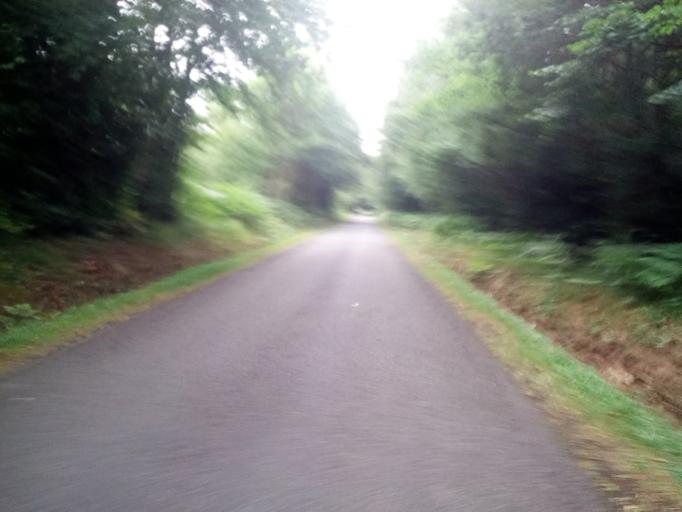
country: FR
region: Lower Normandy
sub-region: Departement du Calvados
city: Clinchamps-sur-Orne
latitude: 49.0218
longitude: -0.3979
